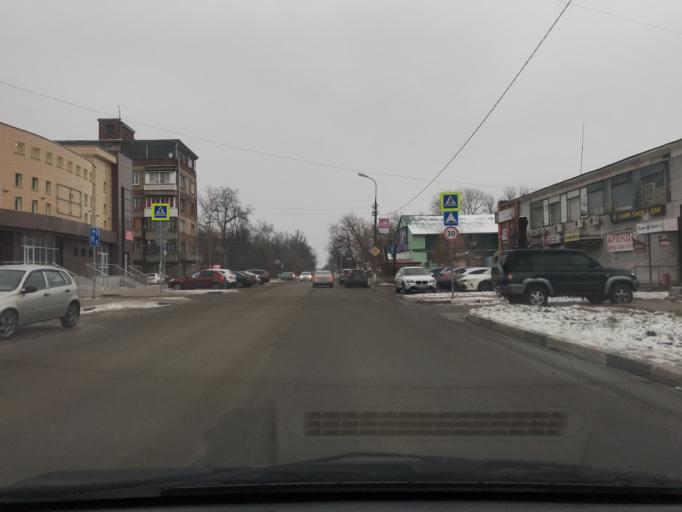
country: RU
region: Moskovskaya
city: Elektrostal'
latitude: 55.7948
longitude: 38.4451
